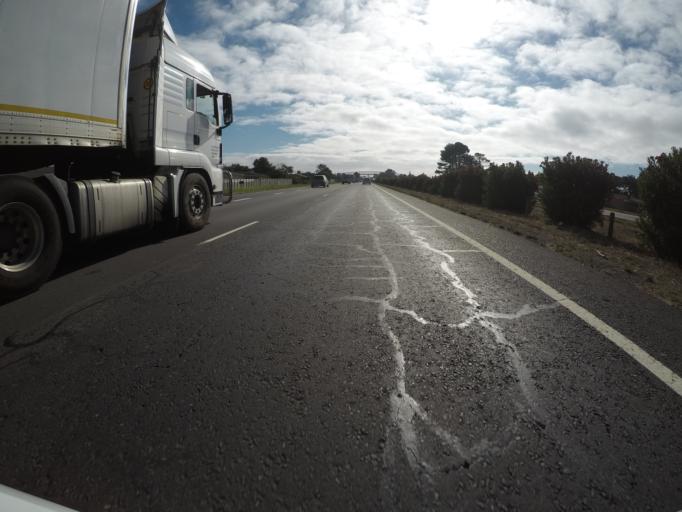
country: ZA
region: Western Cape
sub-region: City of Cape Town
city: Kraaifontein
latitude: -33.8432
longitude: 18.7180
